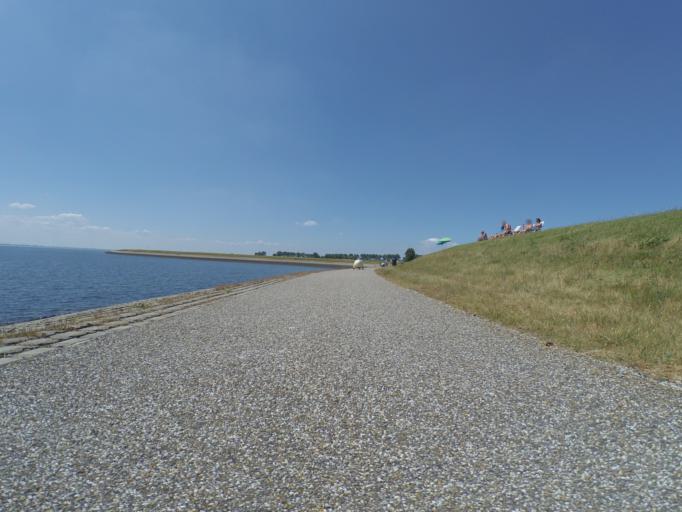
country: NL
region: Zeeland
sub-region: Gemeente Tholen
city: Tholen
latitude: 51.5235
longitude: 4.1528
